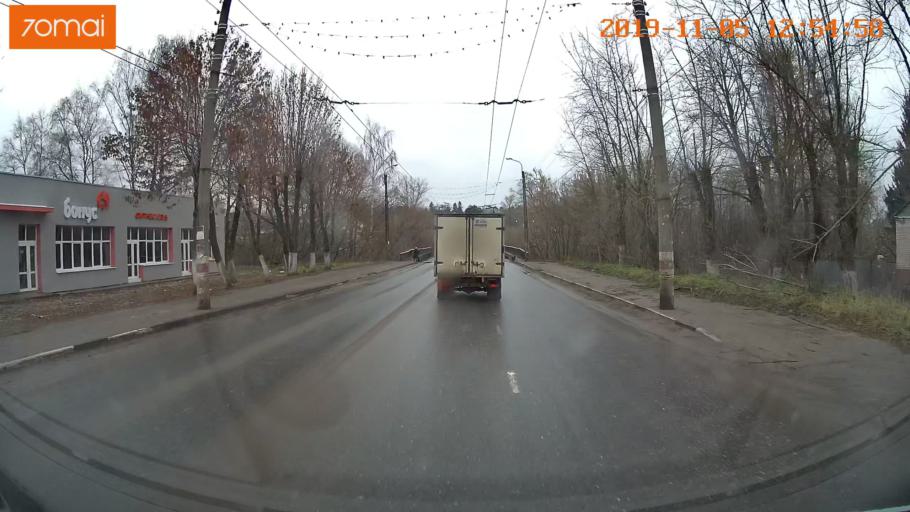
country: RU
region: Ivanovo
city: Kokhma
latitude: 56.9299
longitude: 41.0914
